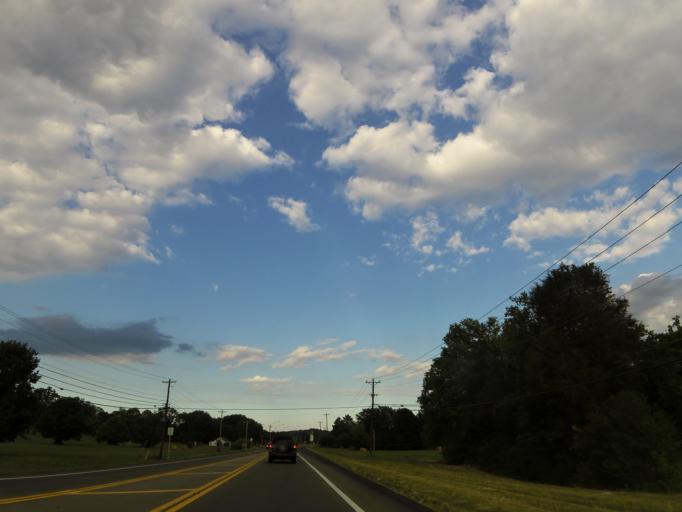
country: US
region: Tennessee
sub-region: Maury County
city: Columbia
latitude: 35.6362
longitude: -86.9775
